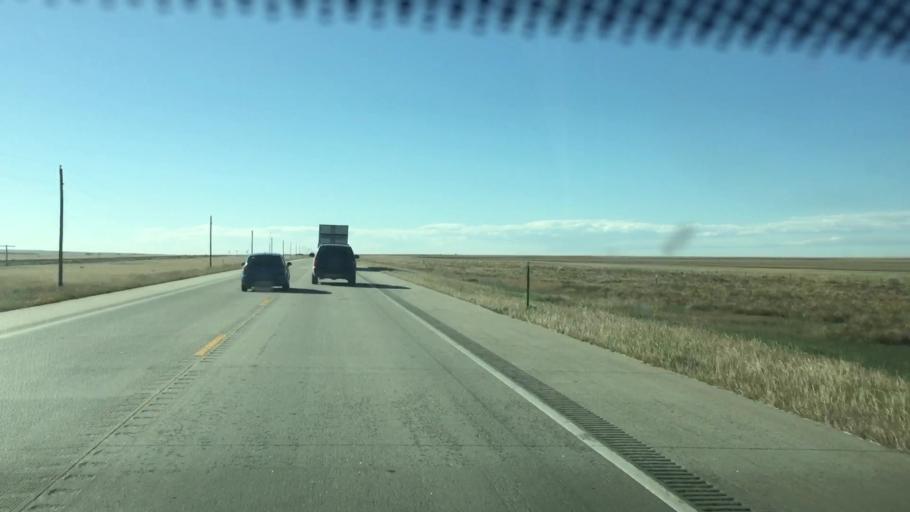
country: US
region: Colorado
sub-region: Kiowa County
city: Eads
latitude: 38.8343
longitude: -103.0630
